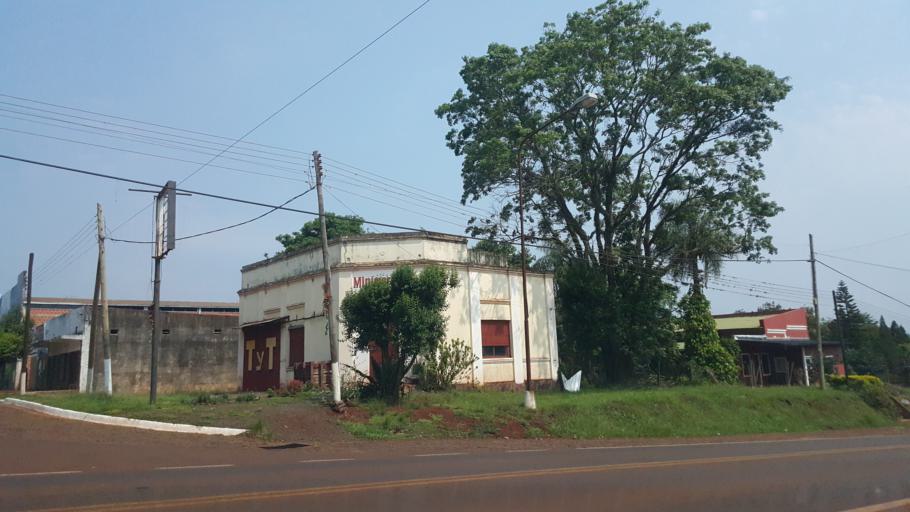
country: AR
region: Misiones
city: Gobernador Roca
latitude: -27.1919
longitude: -55.4708
